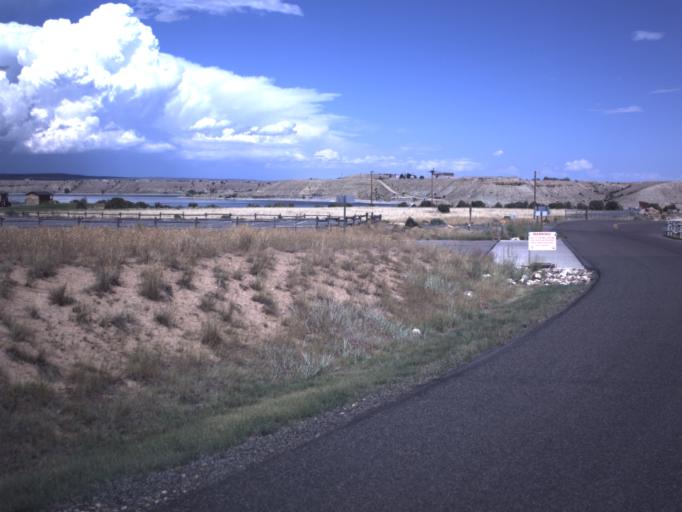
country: US
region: Utah
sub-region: Duchesne County
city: Duchesne
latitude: 40.1887
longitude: -110.4529
